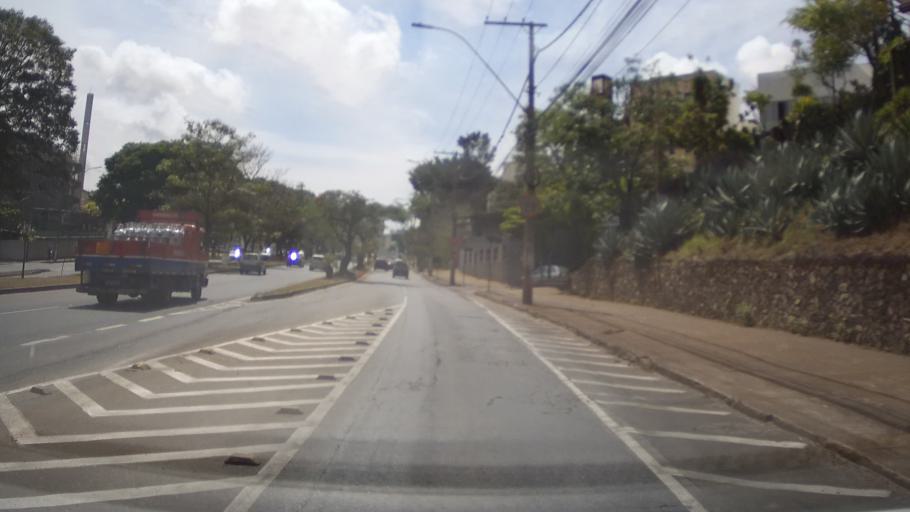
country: BR
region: Minas Gerais
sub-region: Belo Horizonte
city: Belo Horizonte
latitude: -19.9720
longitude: -43.9495
